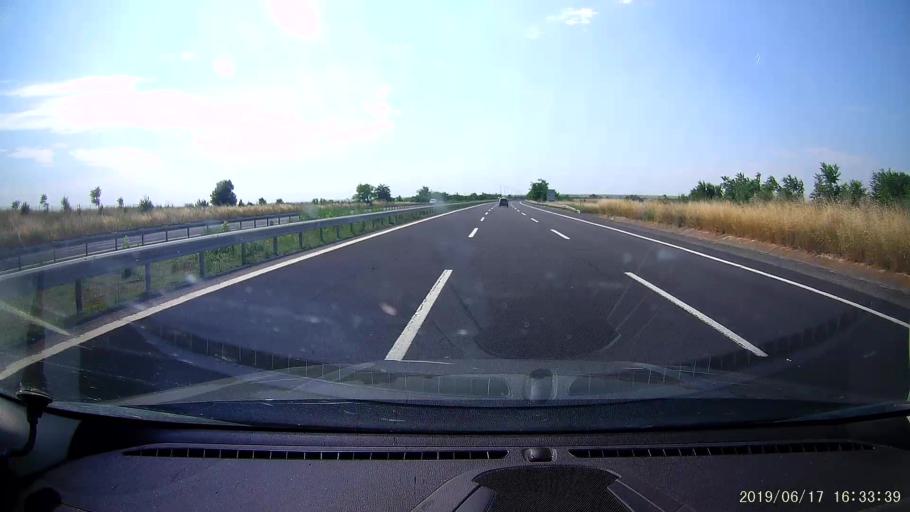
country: TR
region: Kirklareli
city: Buyukkaristiran
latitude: 41.3829
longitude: 27.5664
